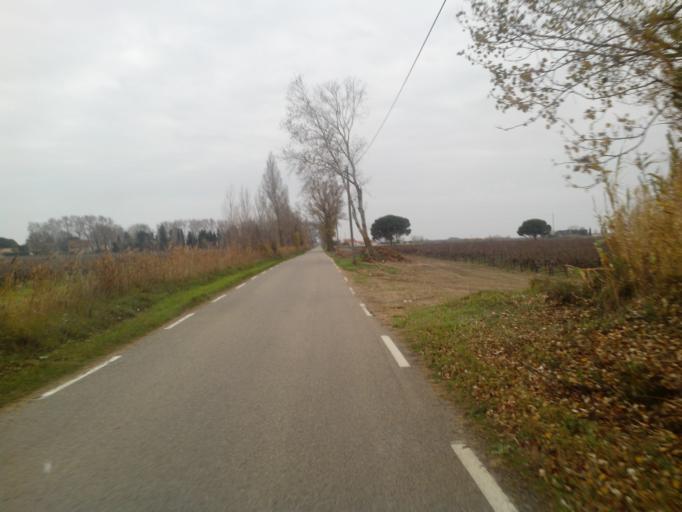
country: FR
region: Languedoc-Roussillon
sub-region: Departement du Gard
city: Vauvert
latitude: 43.5798
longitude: 4.3341
